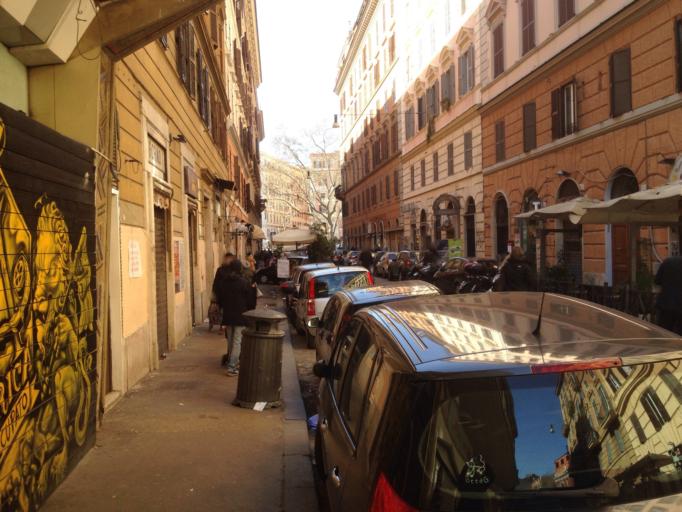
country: VA
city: Vatican City
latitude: 41.8876
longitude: 12.4711
